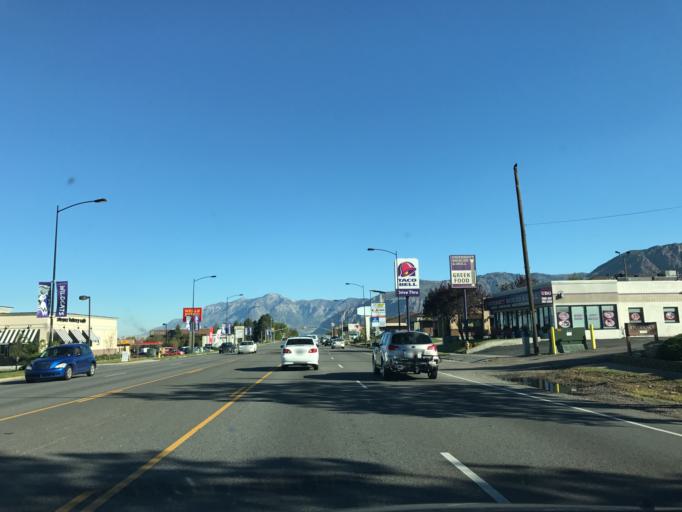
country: US
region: Utah
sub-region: Weber County
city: South Ogden
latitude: 41.1836
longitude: -111.9491
